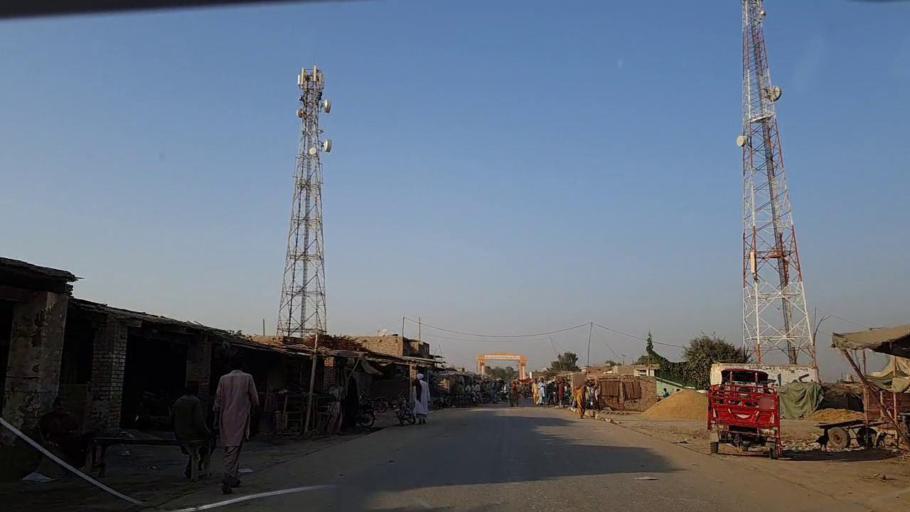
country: PK
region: Sindh
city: Rustam jo Goth
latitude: 28.0199
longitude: 68.8122
